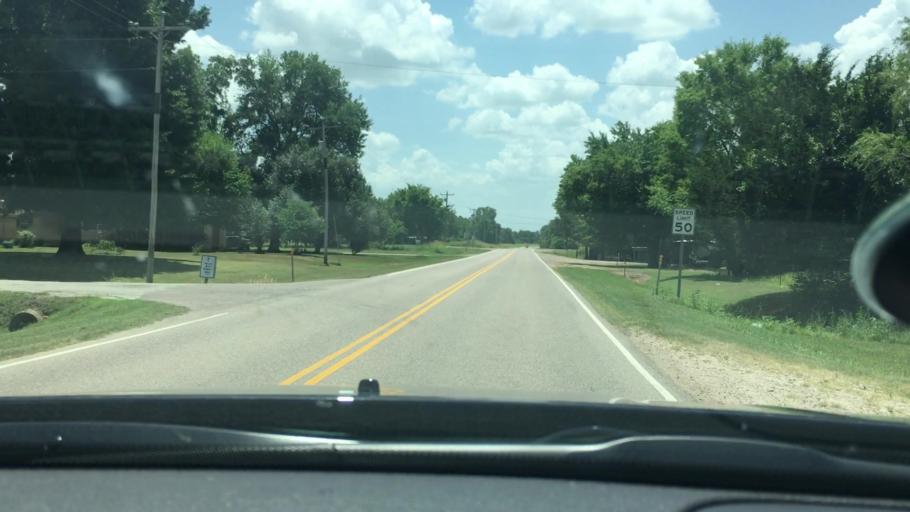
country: US
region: Oklahoma
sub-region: Johnston County
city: Tishomingo
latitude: 34.4909
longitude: -96.6273
